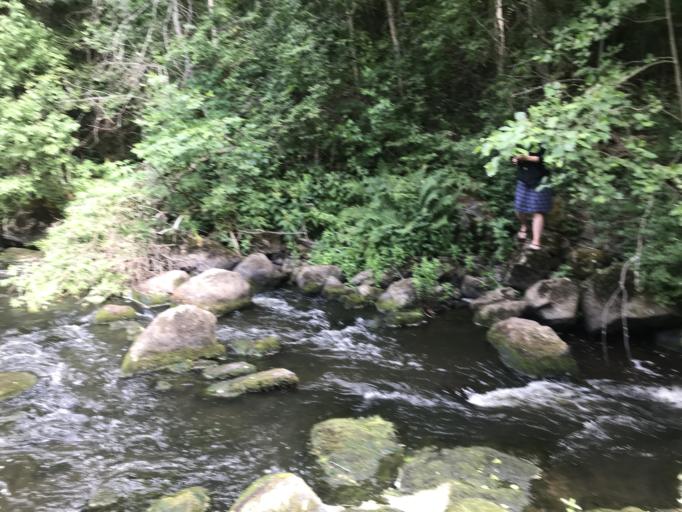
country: FI
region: Uusimaa
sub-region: Helsinki
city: Hyvinge
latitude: 60.5258
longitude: 24.9156
